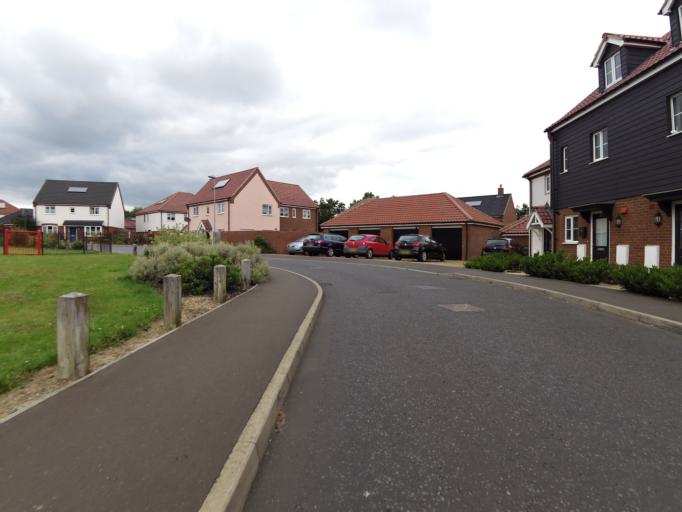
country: GB
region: England
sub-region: Norfolk
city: Diss
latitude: 52.3781
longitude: 1.1264
